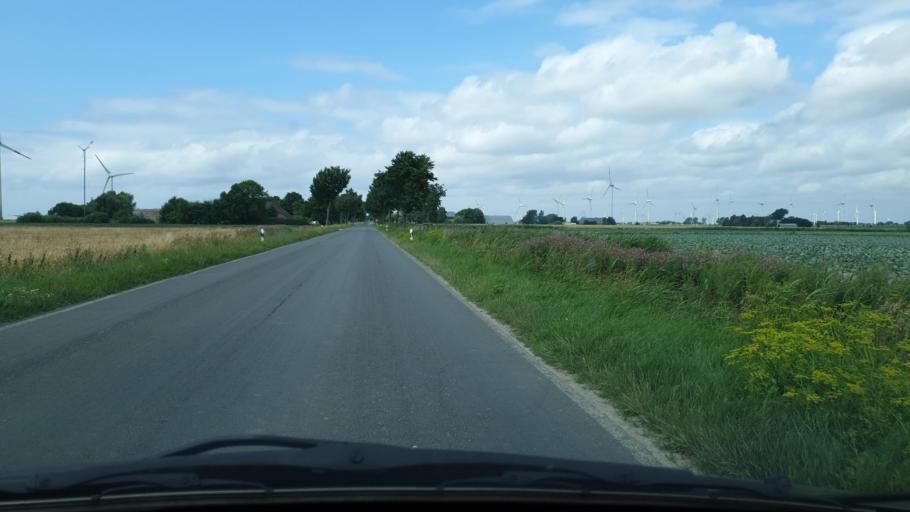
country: DE
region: Schleswig-Holstein
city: Kronprinzenkoog
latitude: 53.9599
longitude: 8.9325
